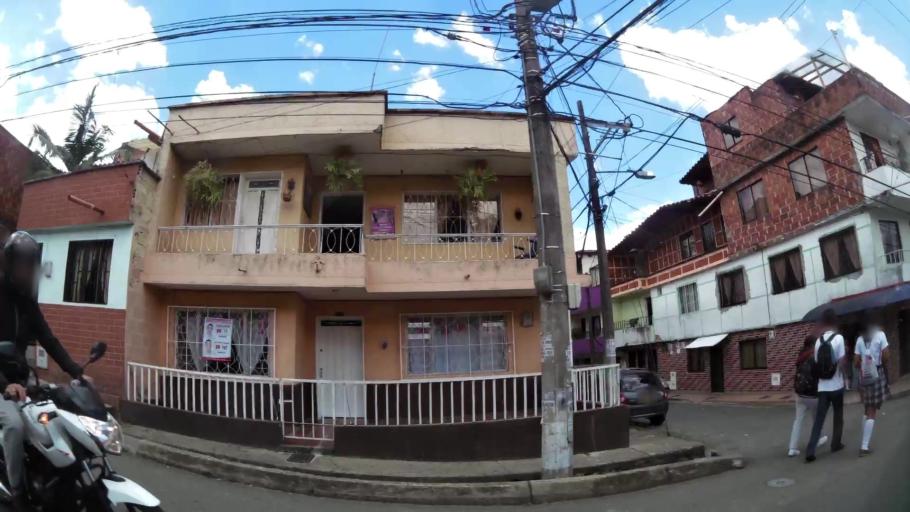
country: CO
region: Antioquia
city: La Estrella
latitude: 6.1558
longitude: -75.6418
